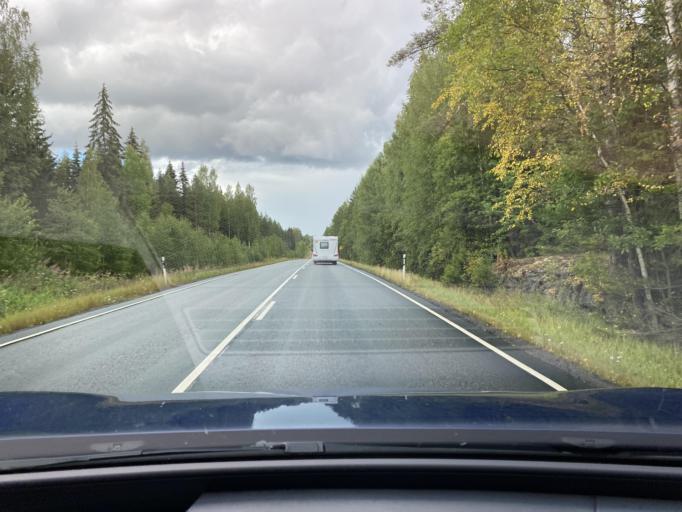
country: FI
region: Pirkanmaa
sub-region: Lounais-Pirkanmaa
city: Mouhijaervi
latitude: 61.5236
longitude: 23.0936
